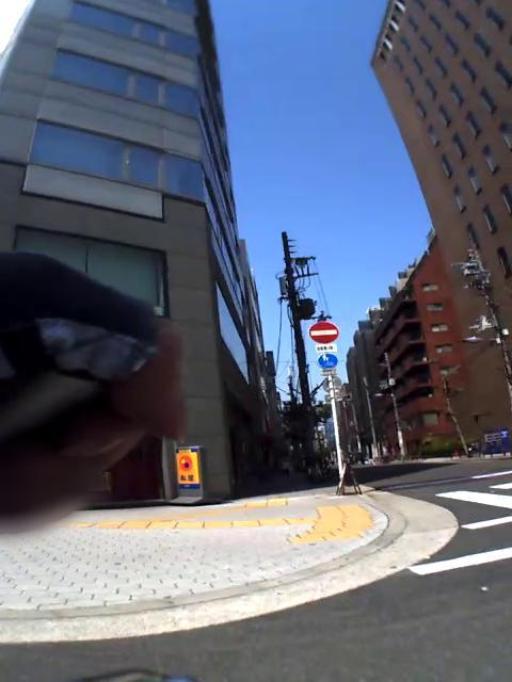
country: JP
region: Osaka
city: Osaka-shi
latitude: 34.6870
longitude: 135.5173
